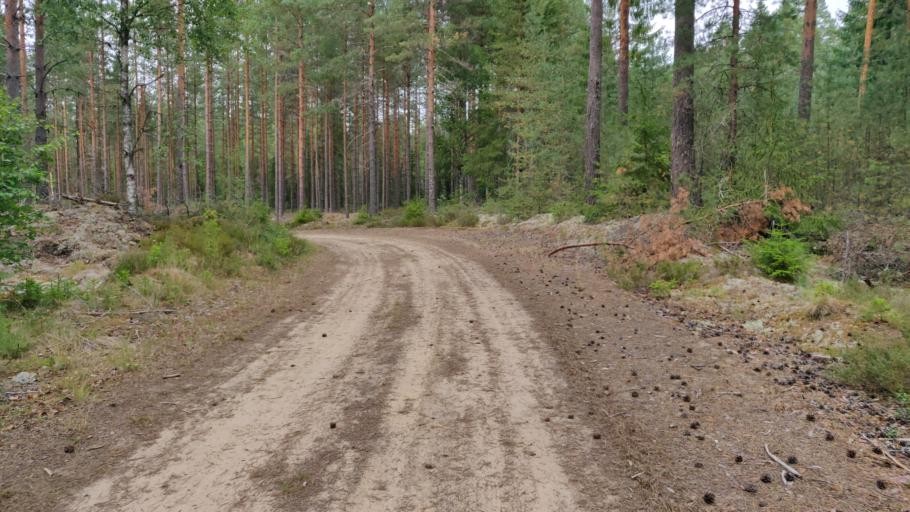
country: SE
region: Vaermland
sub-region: Hagfors Kommun
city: Hagfors
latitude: 60.0166
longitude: 13.5585
